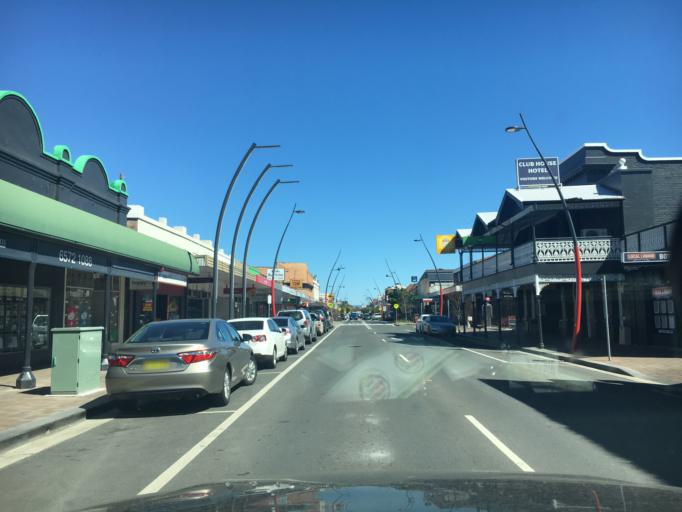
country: AU
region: New South Wales
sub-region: Singleton
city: Singleton
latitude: -32.5641
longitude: 151.1683
